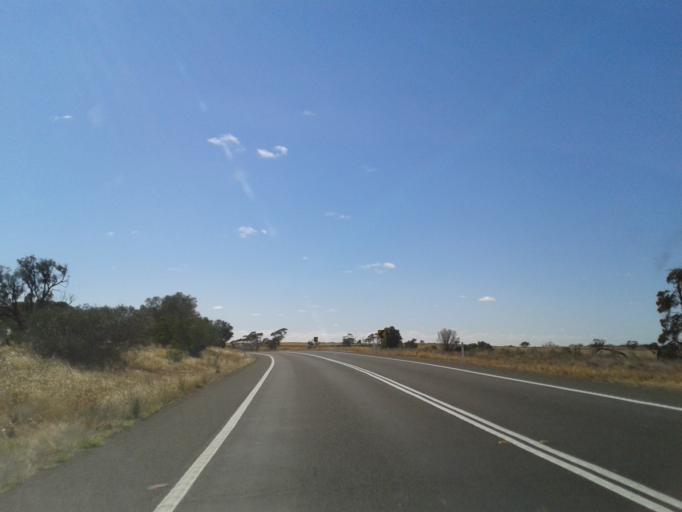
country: AU
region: South Australia
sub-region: Renmark Paringa
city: Renmark
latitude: -34.2753
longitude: 141.2911
